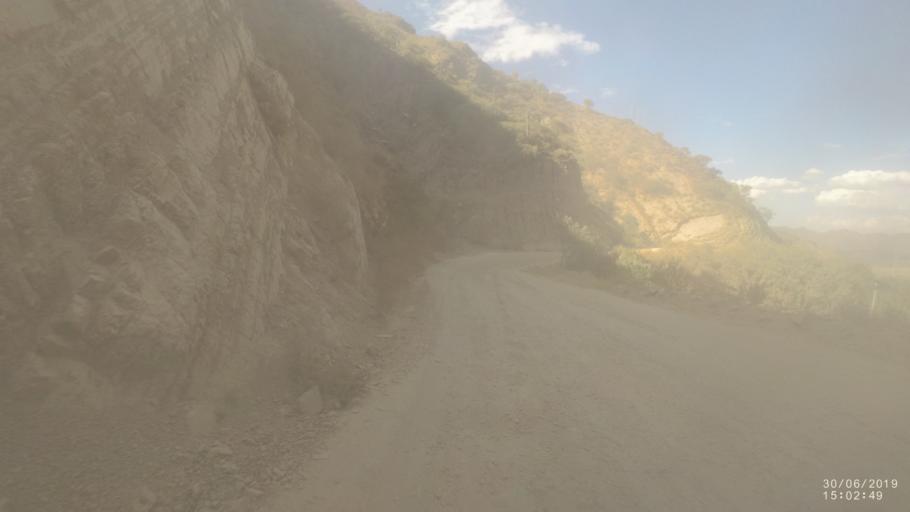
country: BO
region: Cochabamba
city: Irpa Irpa
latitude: -17.7318
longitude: -66.3300
